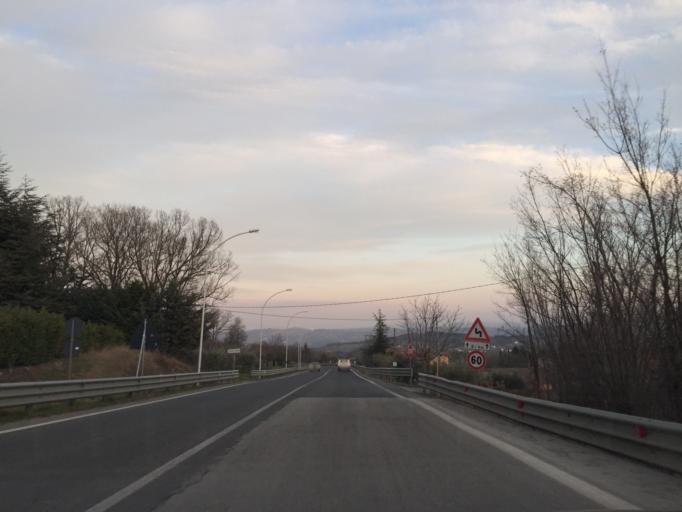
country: IT
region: Molise
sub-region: Provincia di Campobasso
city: Campobasso
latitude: 41.5609
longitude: 14.6881
